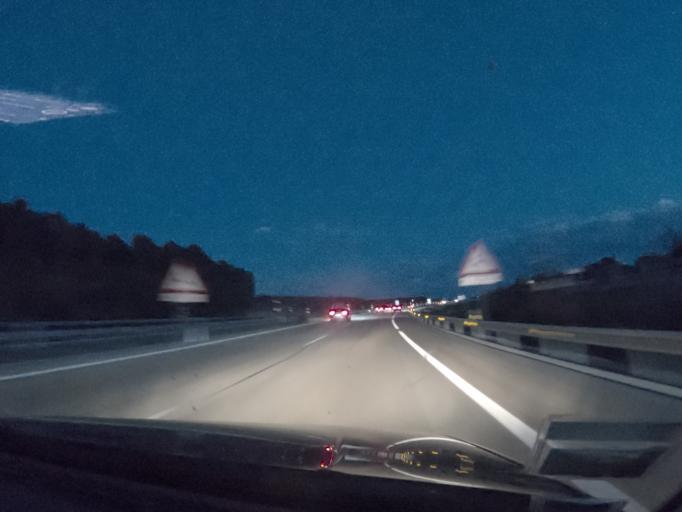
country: ES
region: Castille and Leon
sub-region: Provincia de Leon
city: Villagaton
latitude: 42.5918
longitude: -6.2183
